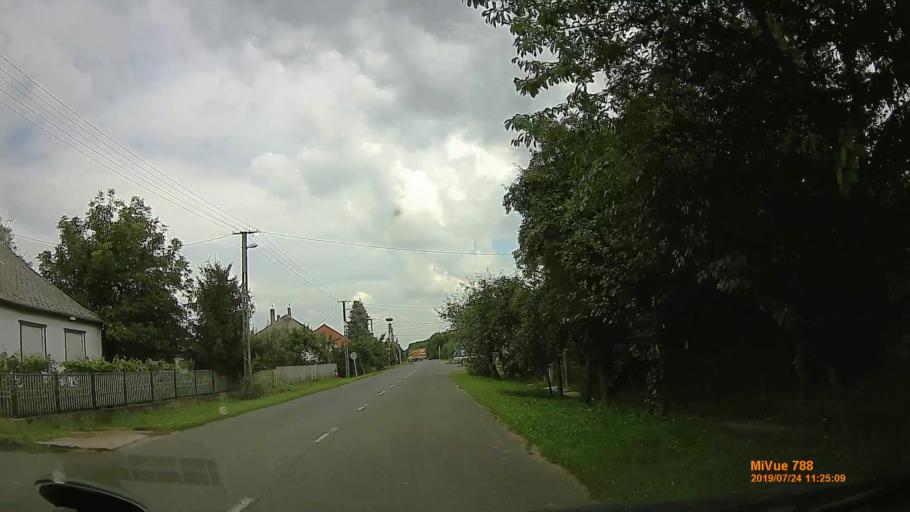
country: HU
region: Szabolcs-Szatmar-Bereg
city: Tarpa
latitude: 48.2020
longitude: 22.4450
